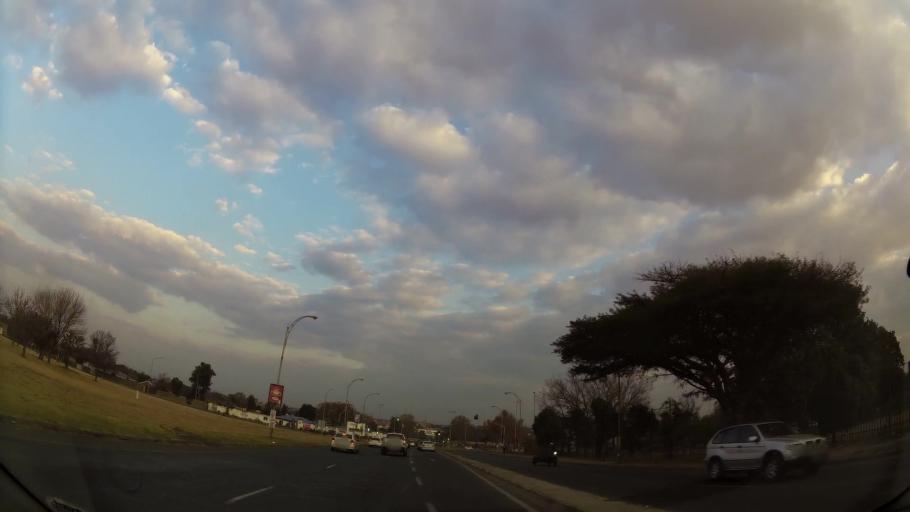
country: ZA
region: Gauteng
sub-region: Ekurhuleni Metropolitan Municipality
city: Benoni
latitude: -26.1767
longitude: 28.3107
